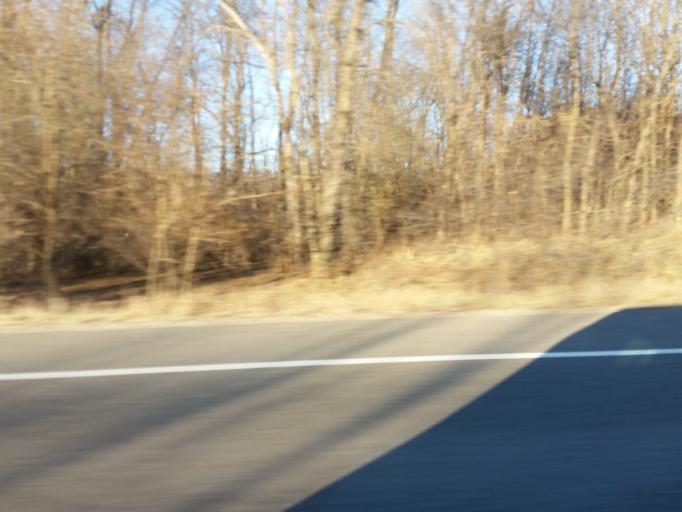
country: US
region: Minnesota
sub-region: Washington County
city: Stillwater
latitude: 45.0792
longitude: -92.8340
